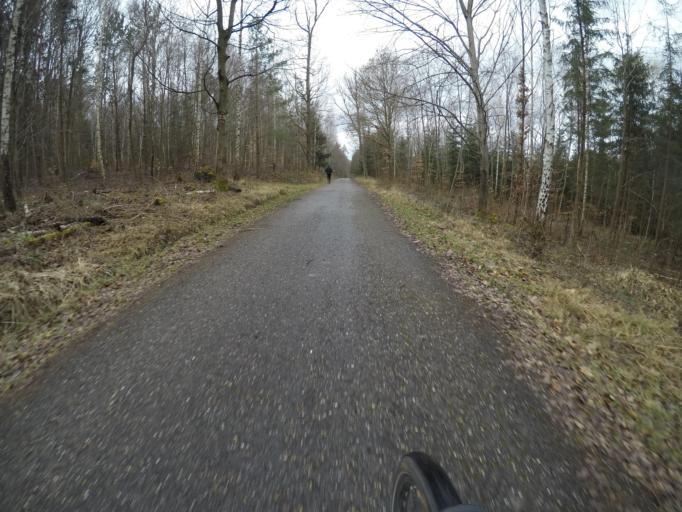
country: DE
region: Baden-Wuerttemberg
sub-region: Regierungsbezirk Stuttgart
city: Sindelfingen
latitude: 48.7227
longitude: 9.0372
